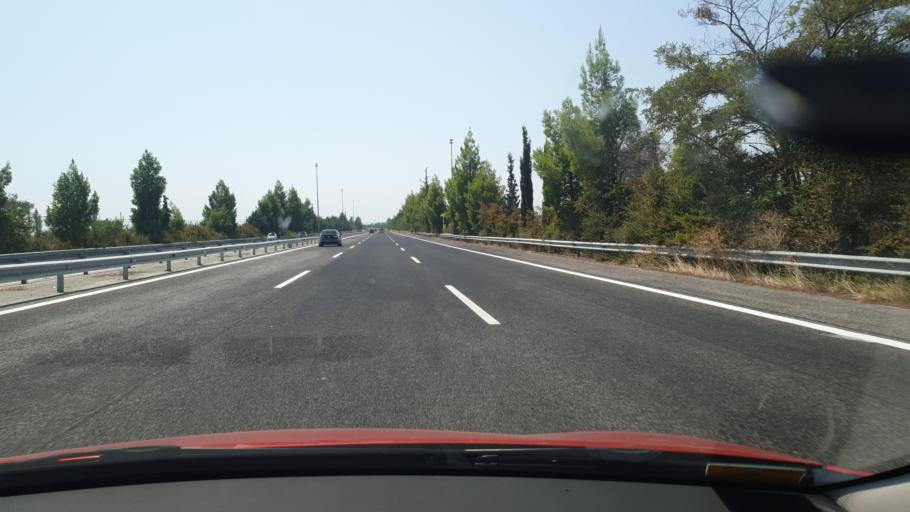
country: GR
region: Thessaly
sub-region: Nomos Larisis
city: Makrychori
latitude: 39.7656
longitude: 22.4814
